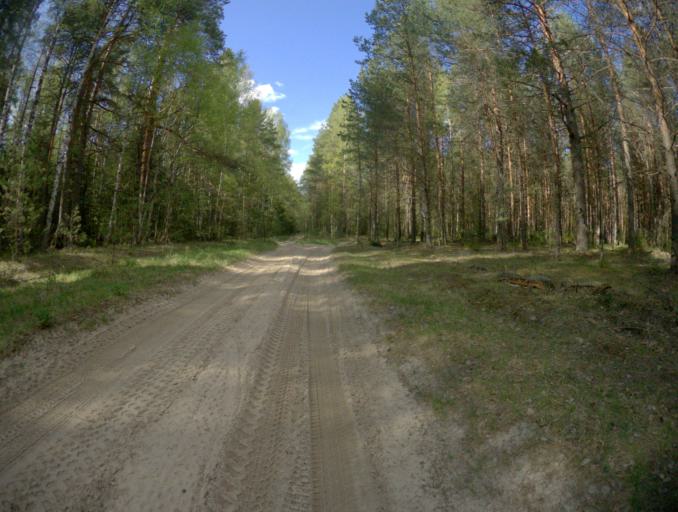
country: RU
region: Vladimir
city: Golovino
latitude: 55.9080
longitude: 40.4426
